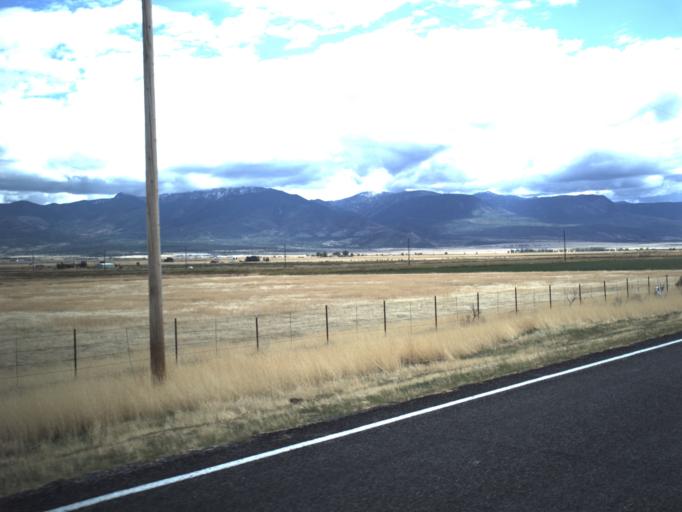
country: US
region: Utah
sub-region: Millard County
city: Fillmore
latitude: 38.9833
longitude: -112.4099
